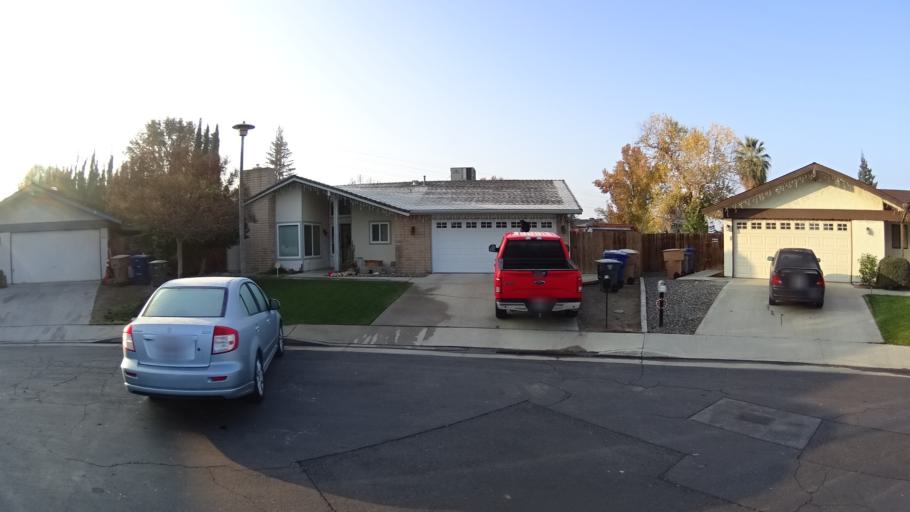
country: US
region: California
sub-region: Kern County
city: Greenacres
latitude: 35.3192
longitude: -119.0758
